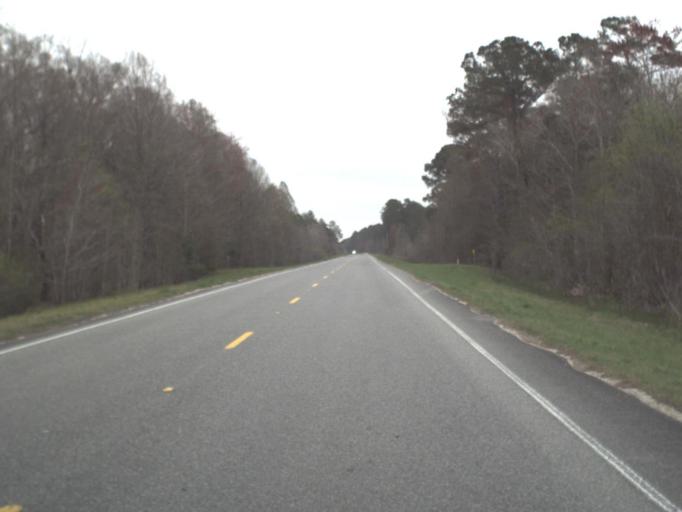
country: US
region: Florida
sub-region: Leon County
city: Woodville
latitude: 30.1919
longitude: -84.0897
